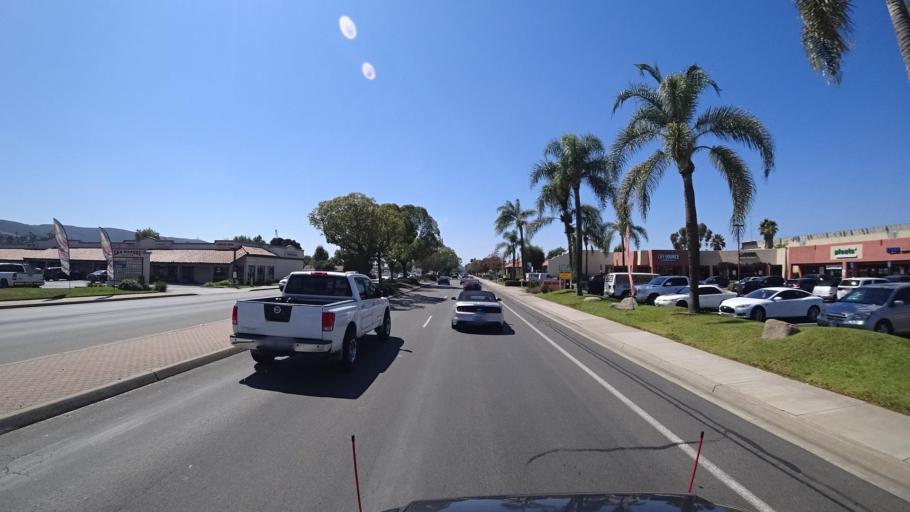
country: US
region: California
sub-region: San Diego County
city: San Marcos
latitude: 33.1362
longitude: -117.1829
